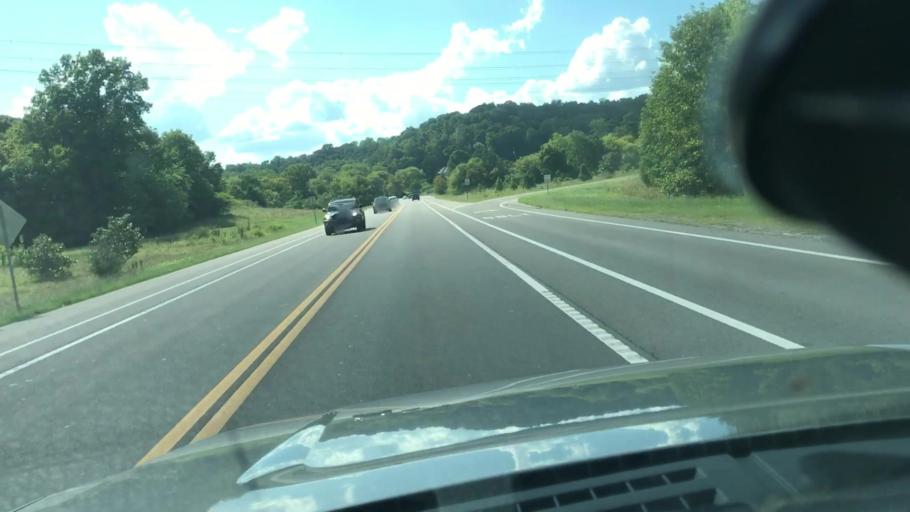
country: US
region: Tennessee
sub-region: Cheatham County
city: Pegram
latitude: 36.0346
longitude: -86.9763
